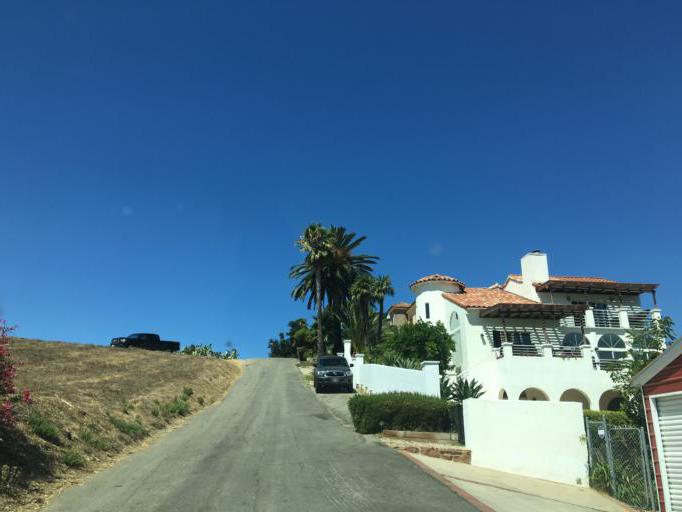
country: US
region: California
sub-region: Los Angeles County
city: Malibu Beach
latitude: 34.0599
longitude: -118.7422
